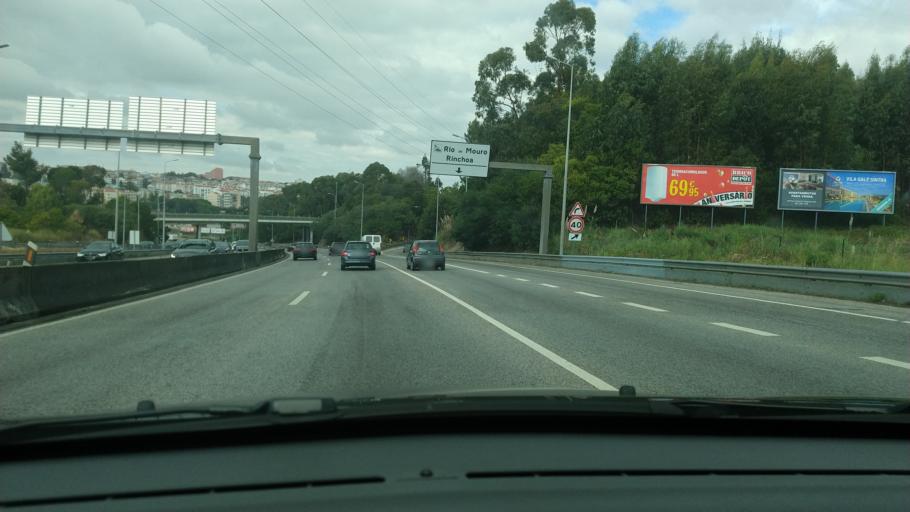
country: PT
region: Lisbon
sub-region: Sintra
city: Rio de Mouro
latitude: 38.7756
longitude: -9.3216
